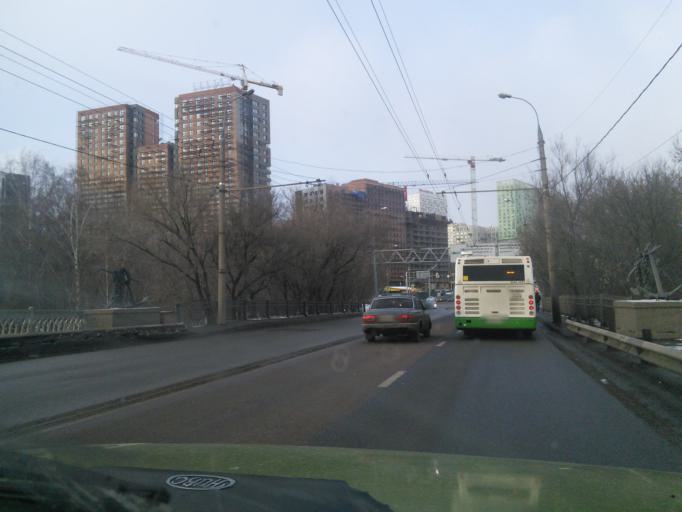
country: RU
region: Moskovskaya
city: Khoroshevo-Mnevniki
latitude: 55.7677
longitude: 37.4752
